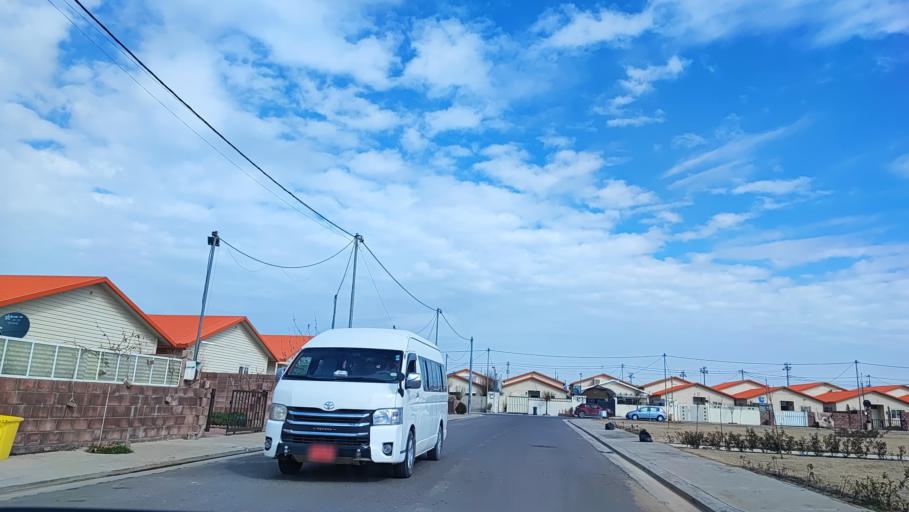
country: IQ
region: Arbil
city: Erbil
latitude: 36.2838
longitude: 44.0690
